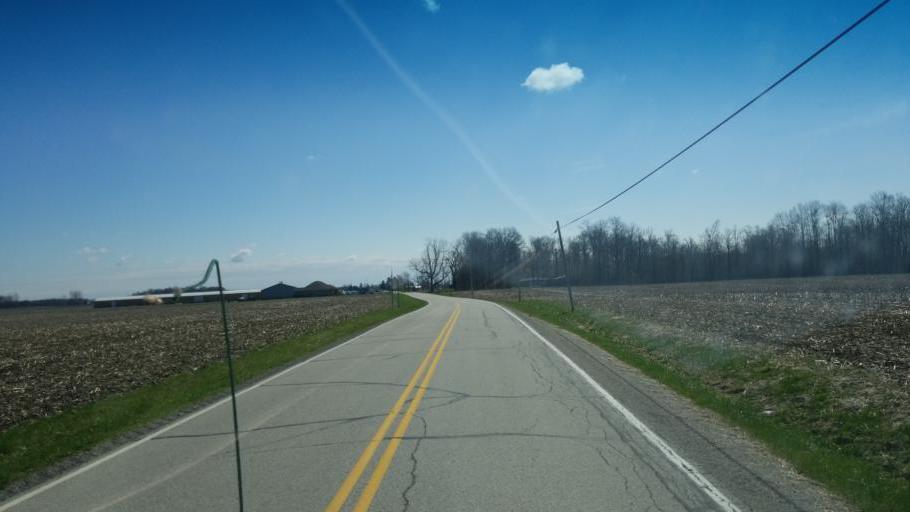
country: US
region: Ohio
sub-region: Crawford County
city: Bucyrus
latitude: 40.8632
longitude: -82.9627
